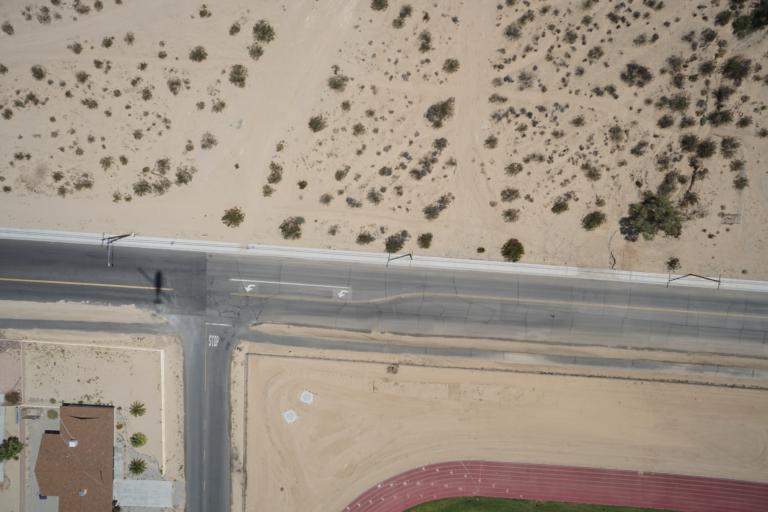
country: US
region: California
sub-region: San Bernardino County
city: Twentynine Palms
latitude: 34.1459
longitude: -116.0716
